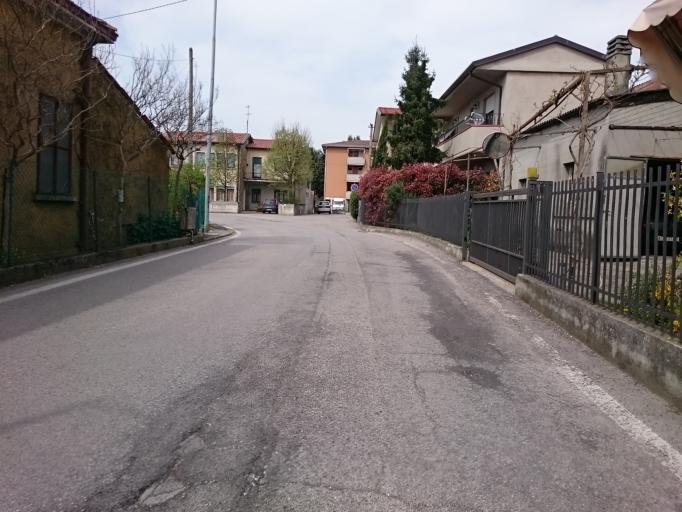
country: IT
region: Veneto
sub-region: Provincia di Padova
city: Anguillara Veneta
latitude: 45.1407
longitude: 11.8866
